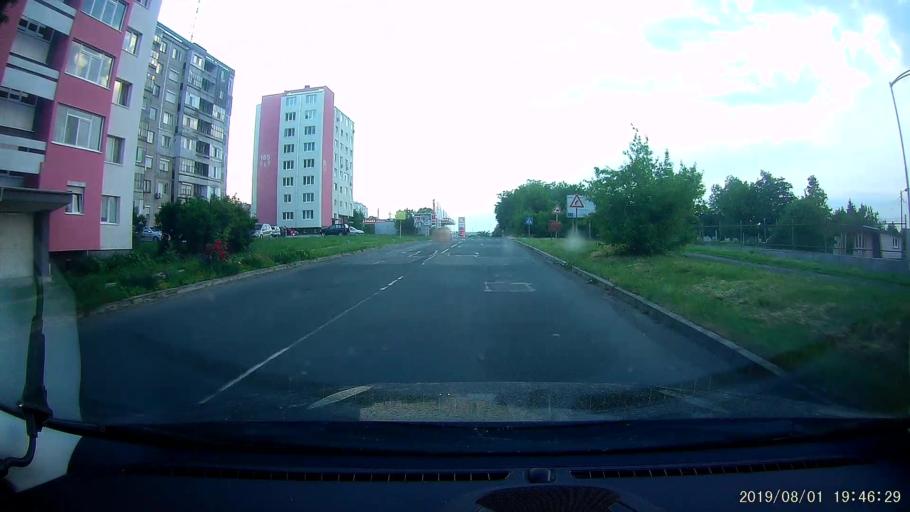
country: BG
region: Burgas
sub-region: Obshtina Karnobat
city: Karnobat
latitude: 42.6500
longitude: 26.9709
